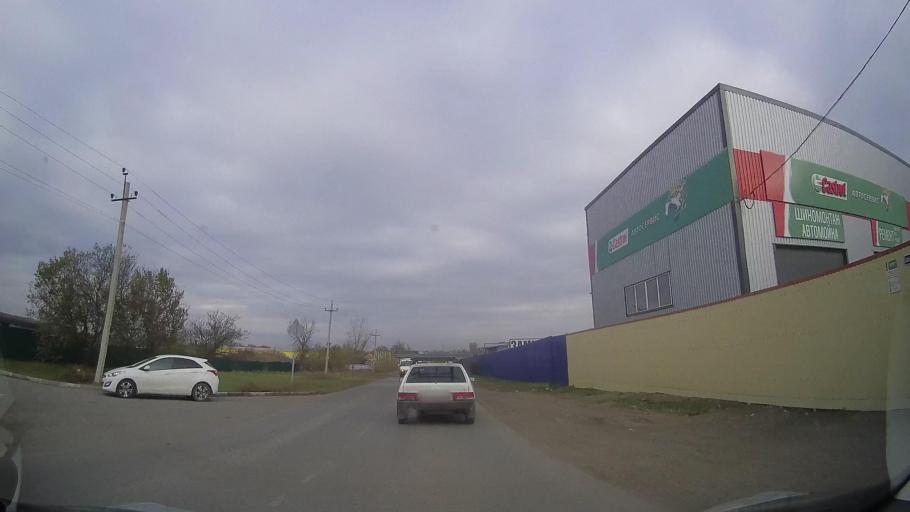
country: RU
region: Rostov
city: Bataysk
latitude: 47.0883
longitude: 39.7656
